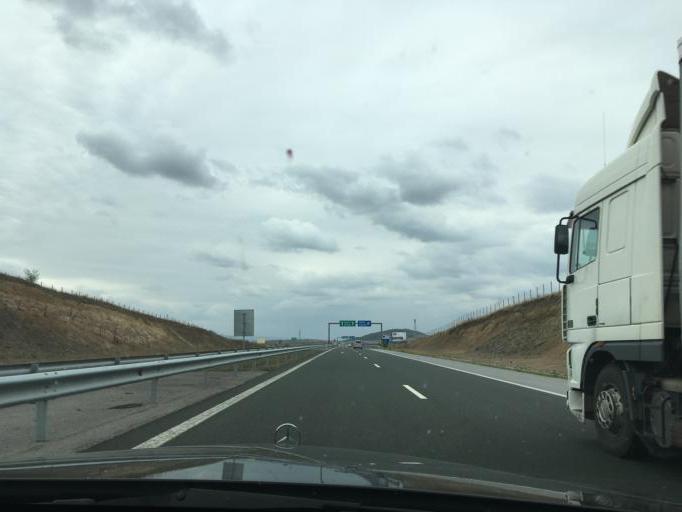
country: BG
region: Yambol
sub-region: Obshtina Yambol
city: Yambol
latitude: 42.5360
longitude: 26.4130
